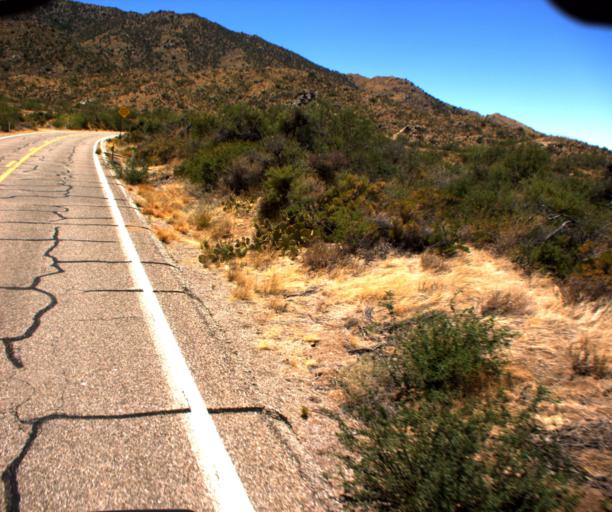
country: US
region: Arizona
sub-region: Pima County
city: Three Points
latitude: 31.9915
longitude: -111.5771
